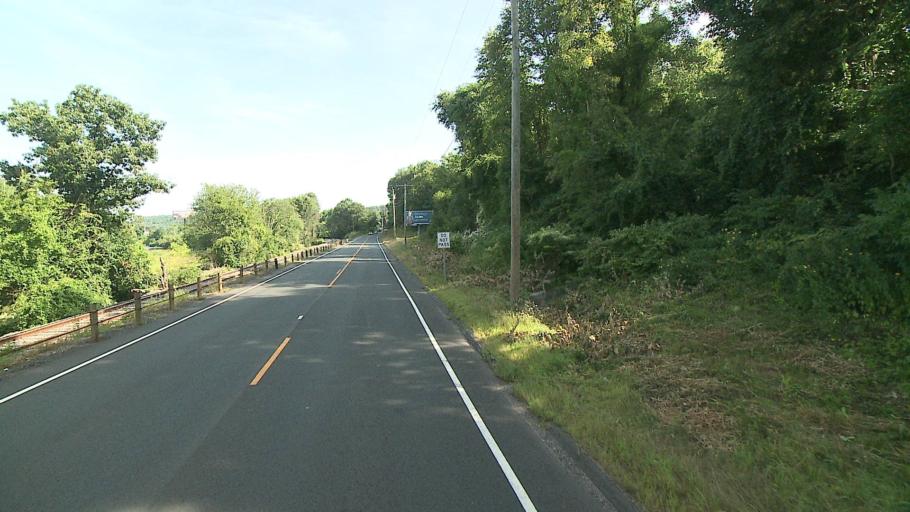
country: US
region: Connecticut
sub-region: New Haven County
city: Waterbury
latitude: 41.5776
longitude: -73.0502
